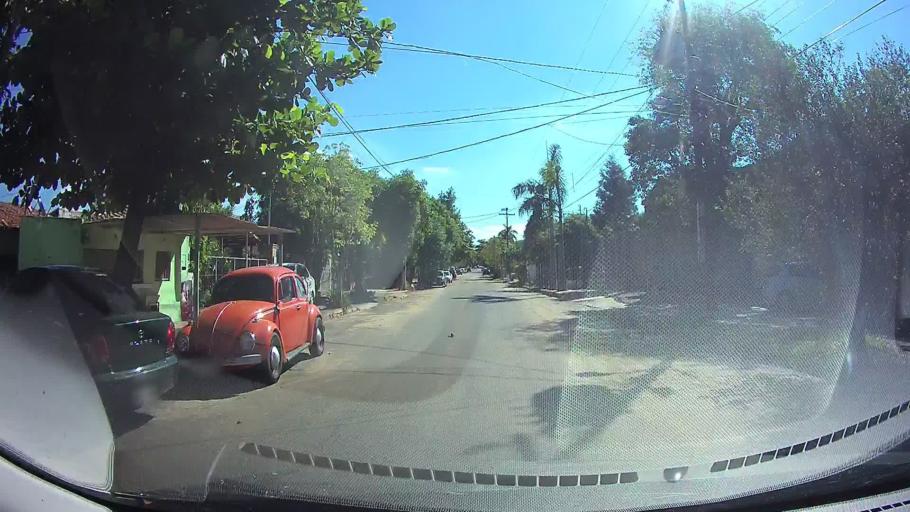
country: PY
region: Central
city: Fernando de la Mora
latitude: -25.3129
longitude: -57.5572
